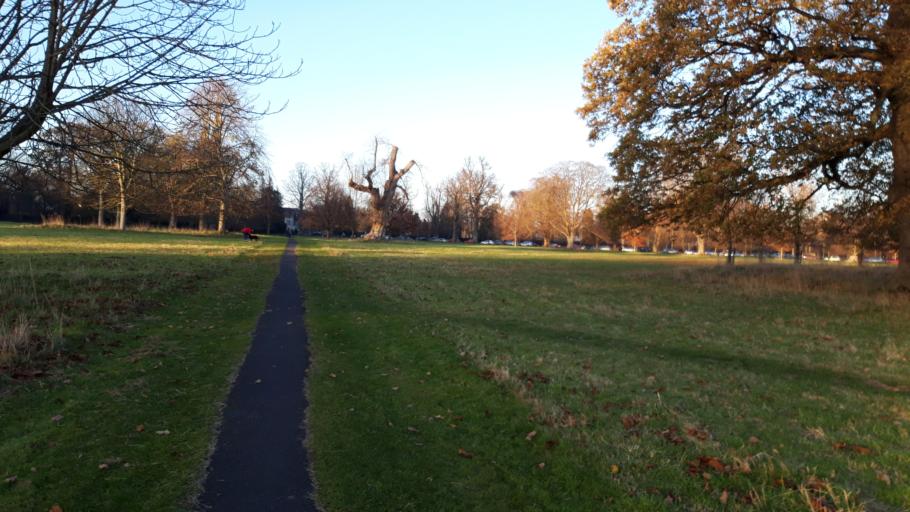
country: IE
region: Leinster
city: Castleknock
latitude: 53.3673
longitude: -6.3481
